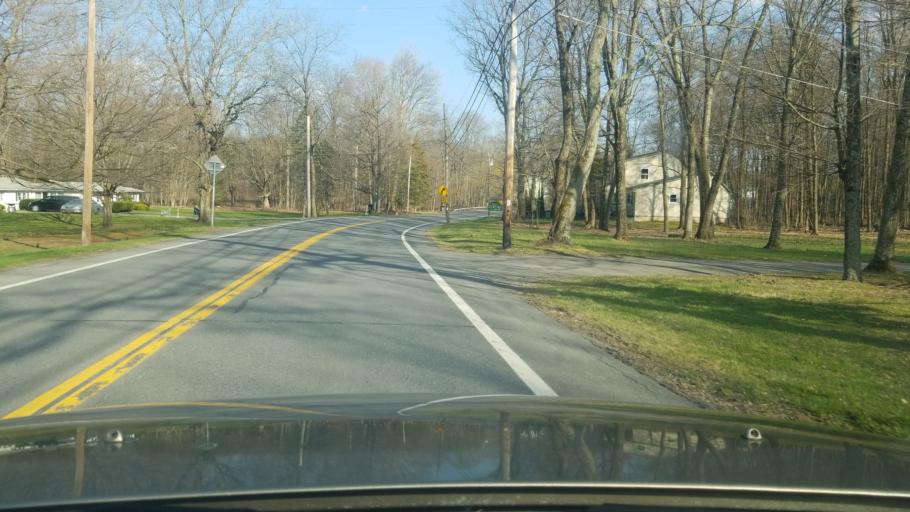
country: US
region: New York
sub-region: Greene County
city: Palenville
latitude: 42.1593
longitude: -73.9996
